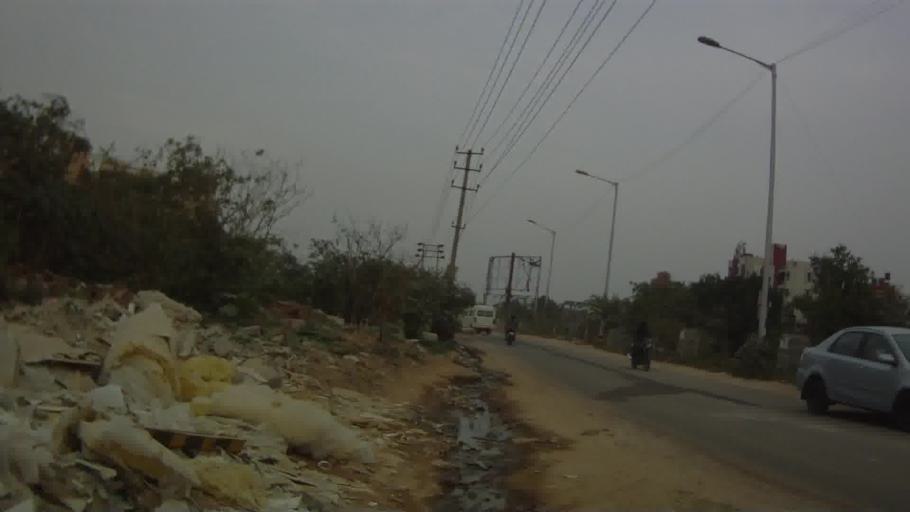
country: IN
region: Karnataka
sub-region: Bangalore Urban
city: Bangalore
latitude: 12.9738
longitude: 77.6986
